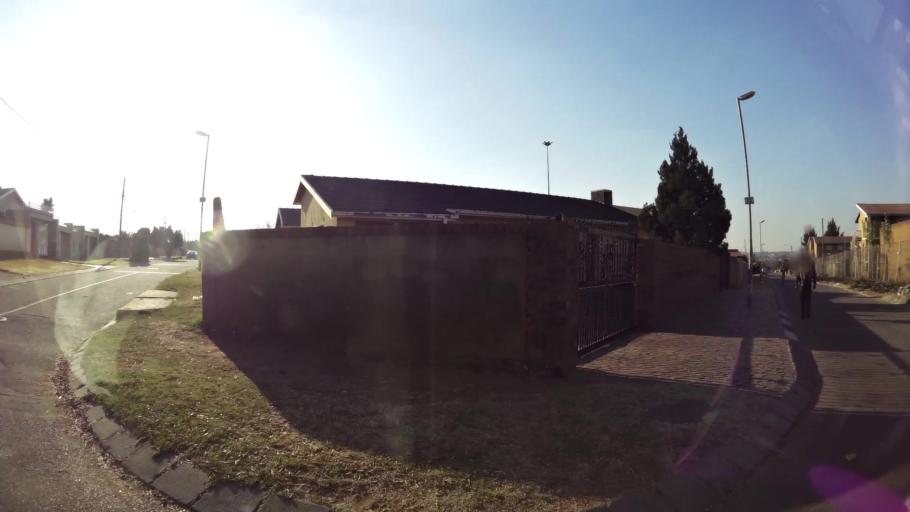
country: ZA
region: Gauteng
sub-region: City of Johannesburg Metropolitan Municipality
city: Soweto
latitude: -26.2679
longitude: 27.8751
